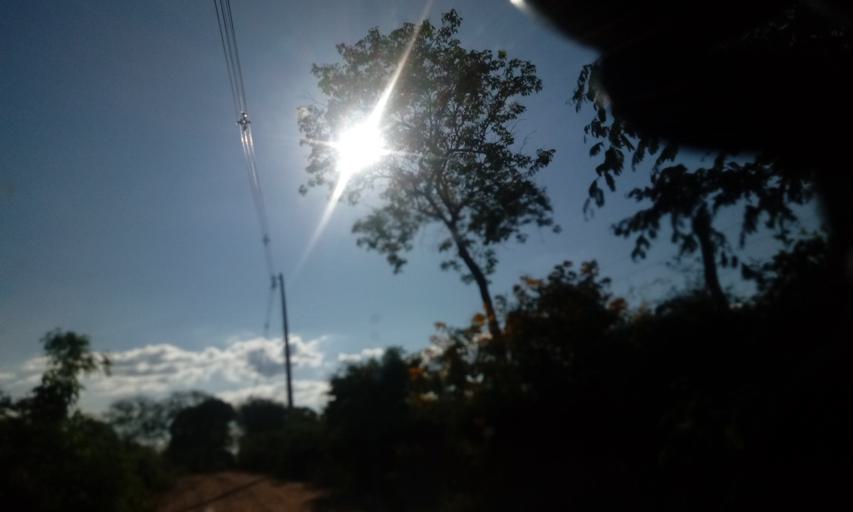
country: BR
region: Bahia
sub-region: Riacho De Santana
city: Riacho de Santana
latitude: -13.8007
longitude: -42.7474
